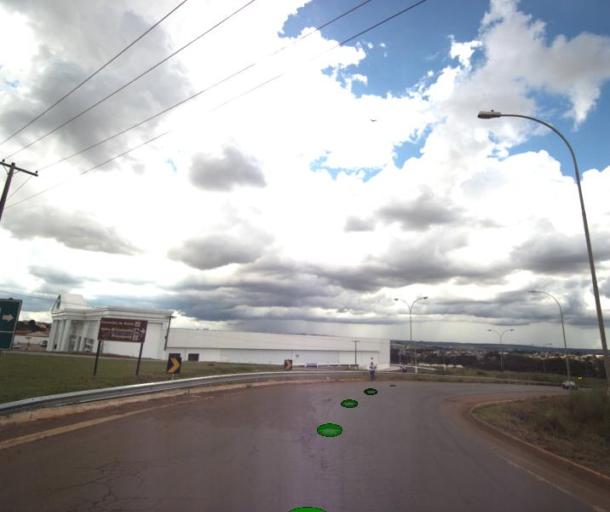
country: BR
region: Goias
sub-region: Anapolis
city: Anapolis
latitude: -16.3532
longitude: -48.9289
